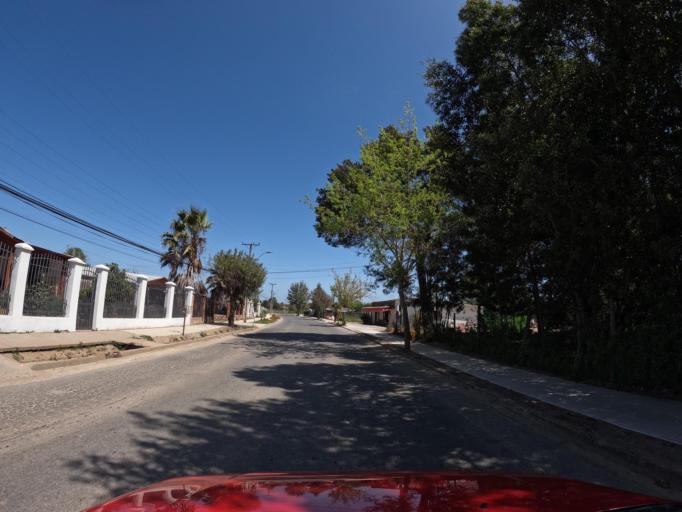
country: CL
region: O'Higgins
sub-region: Provincia de Colchagua
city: Santa Cruz
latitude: -34.7275
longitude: -71.6585
